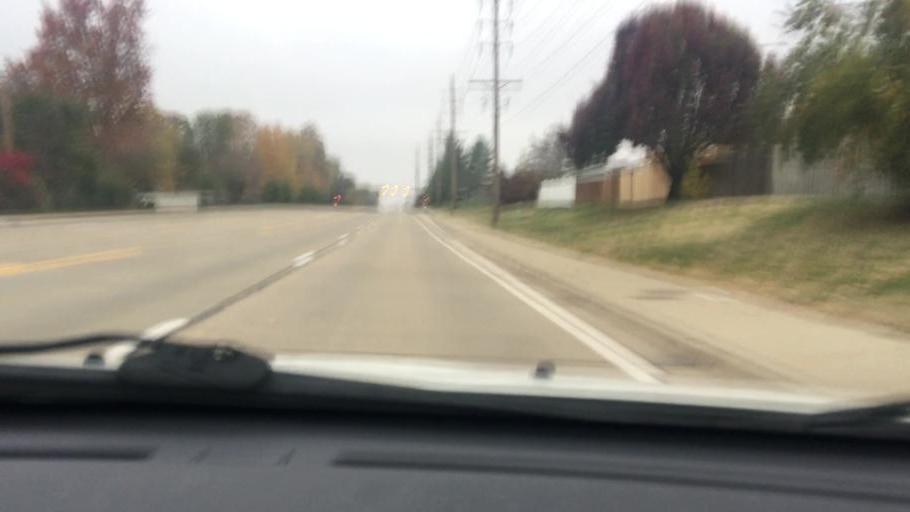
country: US
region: Missouri
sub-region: Saint Charles County
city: O'Fallon
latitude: 38.8218
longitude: -90.6878
